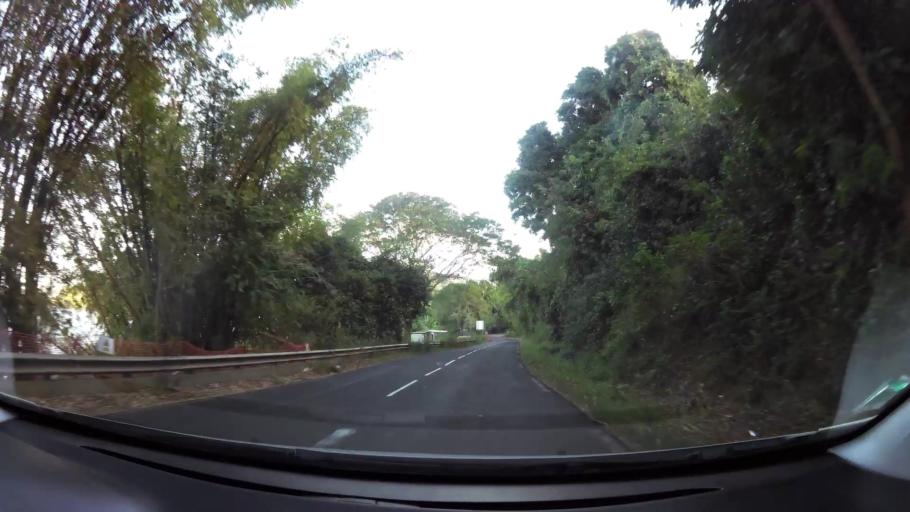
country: YT
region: Dembeni
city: Dembeni
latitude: -12.8234
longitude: 45.1952
